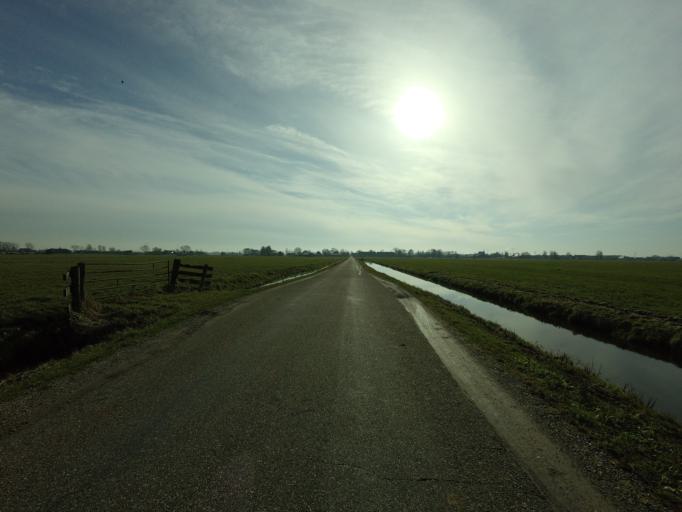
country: NL
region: South Holland
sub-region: Gemeente Sliedrecht
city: Sliedrecht
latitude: 51.8509
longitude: 4.7680
